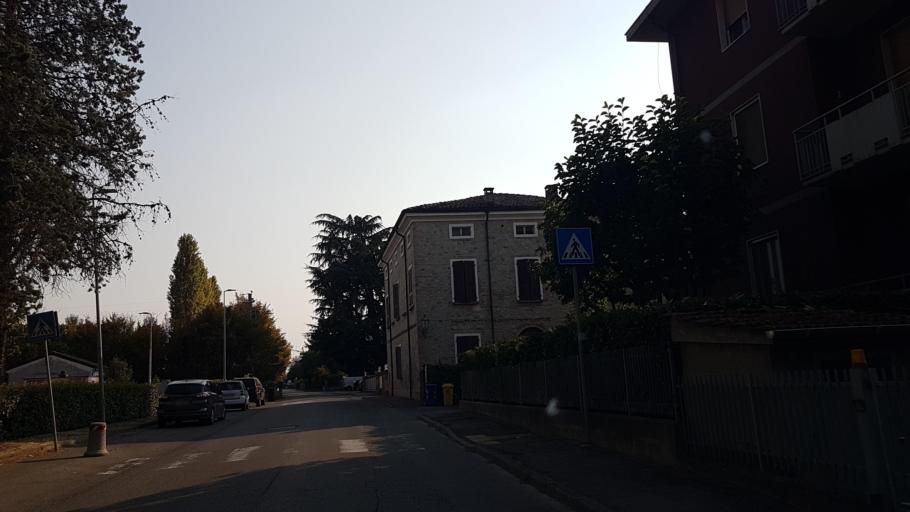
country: IT
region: Emilia-Romagna
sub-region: Provincia di Parma
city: Vicofertile
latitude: 44.7827
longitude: 10.2833
